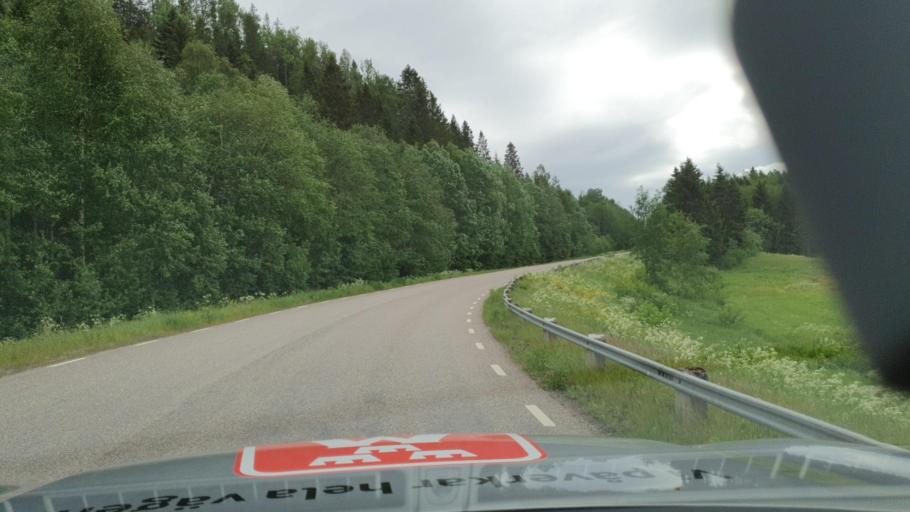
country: SE
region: Vaesternorrland
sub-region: Kramfors Kommun
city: Nordingra
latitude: 62.9022
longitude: 18.3690
